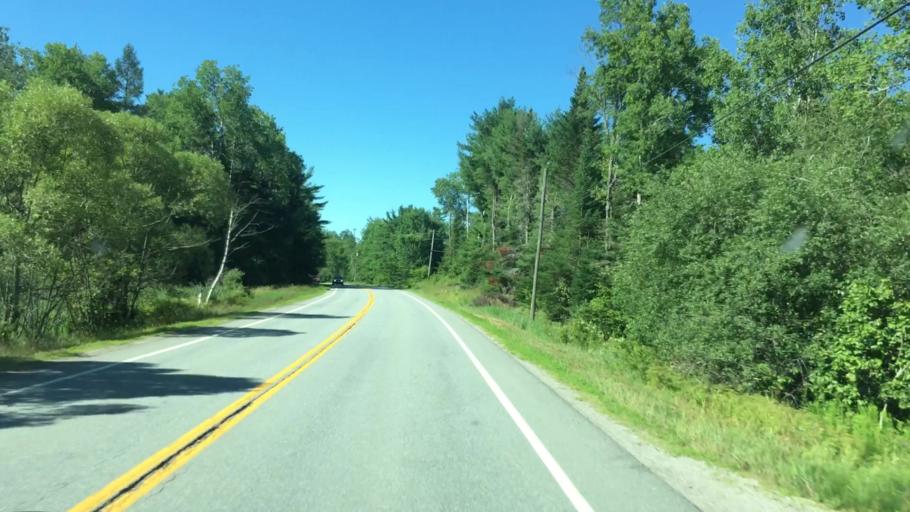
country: US
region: Maine
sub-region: Hancock County
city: Dedham
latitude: 44.6858
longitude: -68.6643
